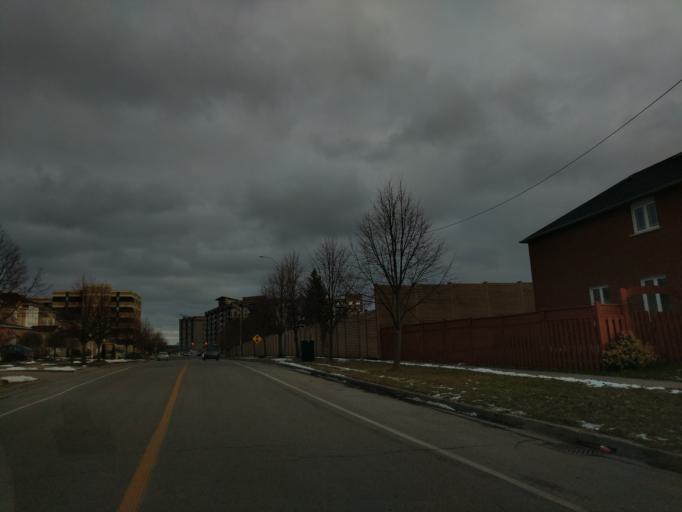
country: CA
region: Ontario
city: Markham
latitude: 43.8471
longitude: -79.2564
